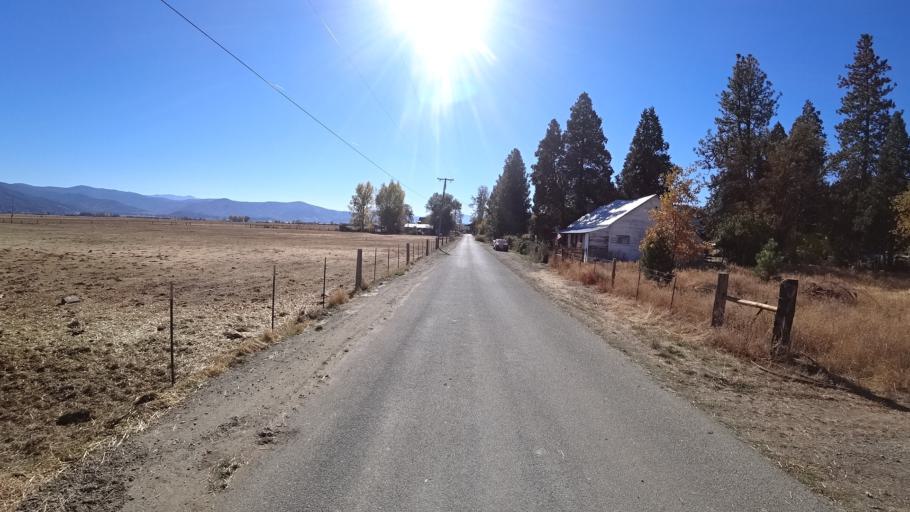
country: US
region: California
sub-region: Siskiyou County
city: Yreka
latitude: 41.5233
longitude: -122.9005
